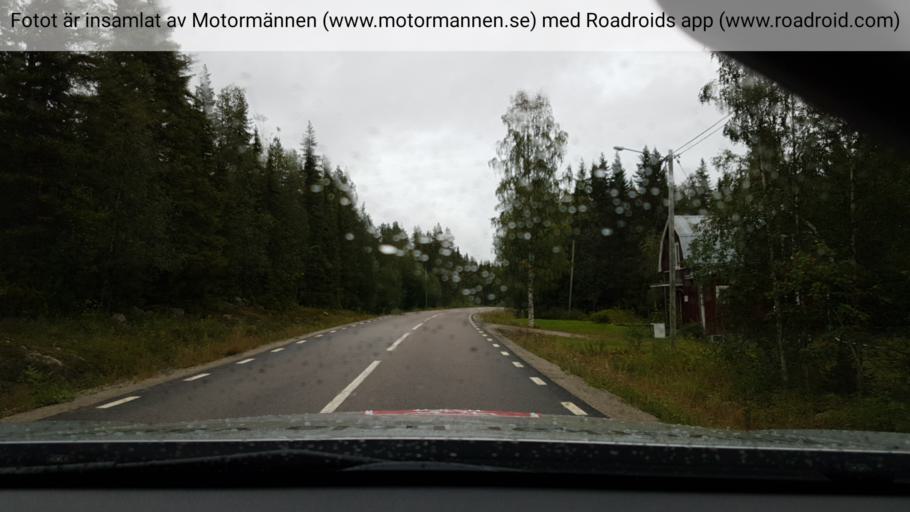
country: SE
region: Vaesterbotten
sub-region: Lycksele Kommun
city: Soderfors
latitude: 64.7115
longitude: 17.7013
